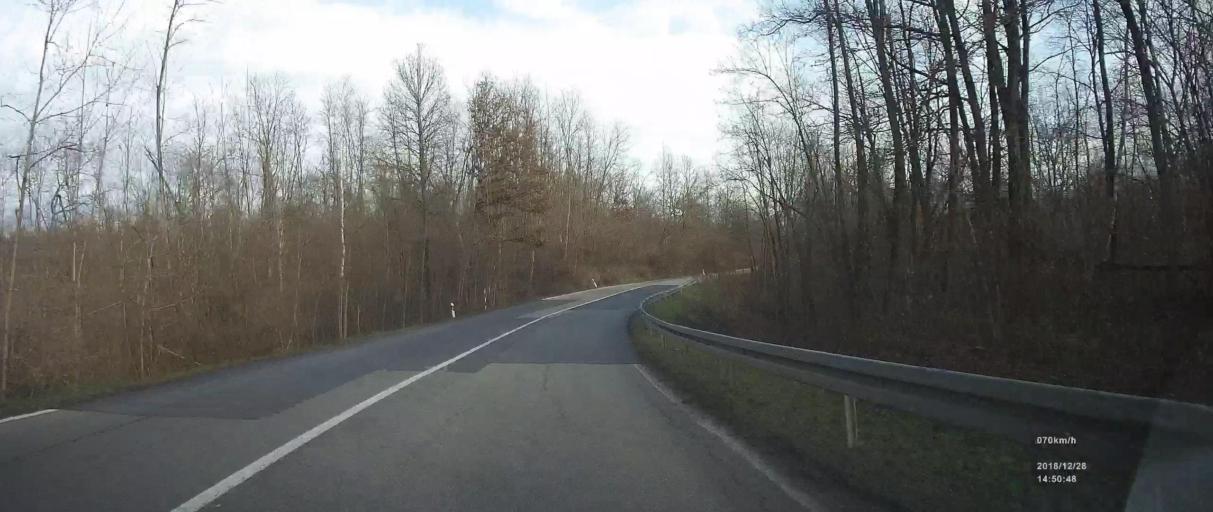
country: HR
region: Karlovacka
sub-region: Grad Karlovac
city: Karlovac
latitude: 45.4466
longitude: 15.3727
